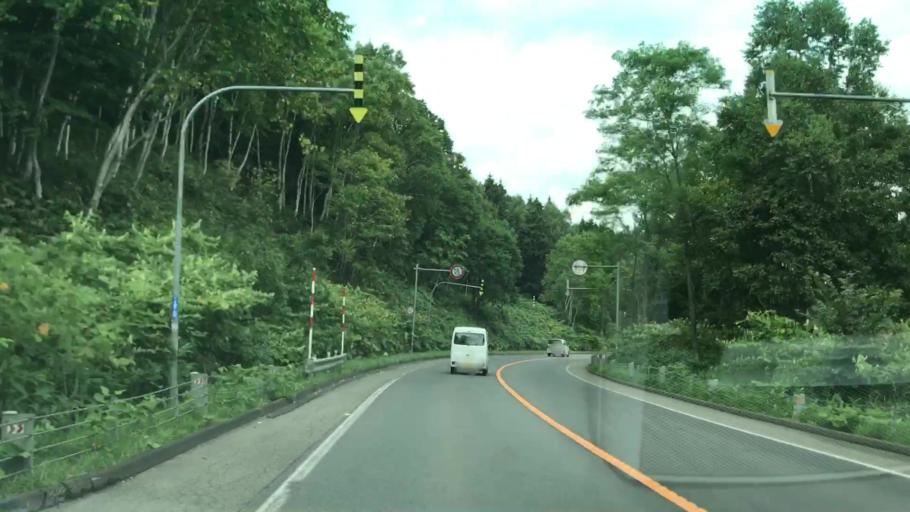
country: JP
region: Hokkaido
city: Niseko Town
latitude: 42.9279
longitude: 140.7156
